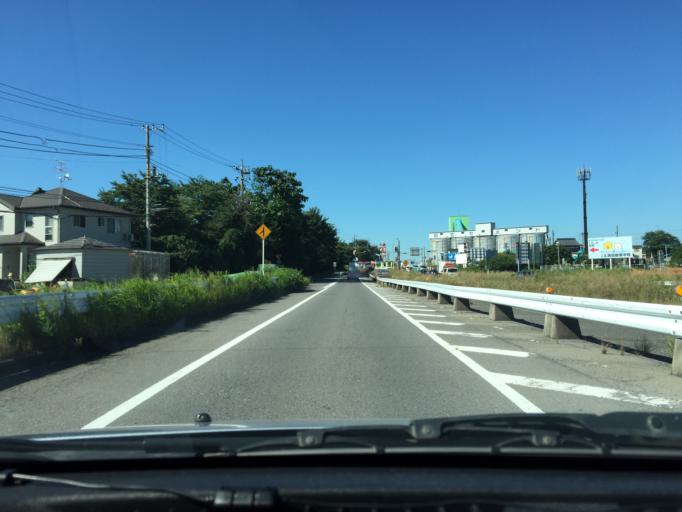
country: JP
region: Ibaraki
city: Naka
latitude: 36.0555
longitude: 140.1758
